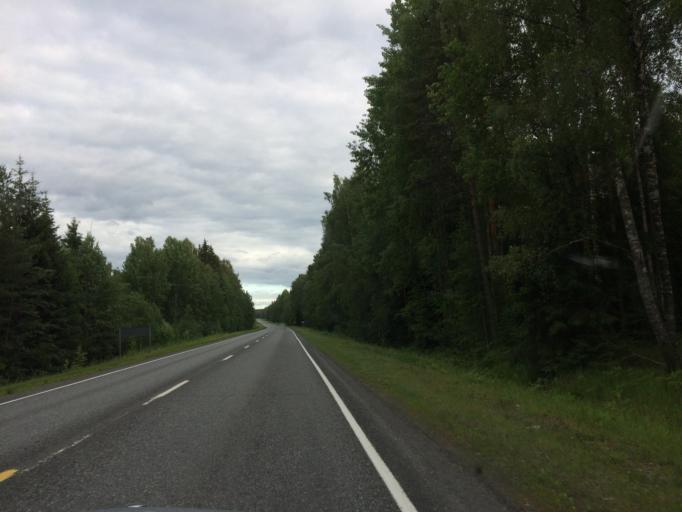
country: FI
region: Haeme
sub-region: Haemeenlinna
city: Haemeenlinna
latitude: 60.9391
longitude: 24.5213
